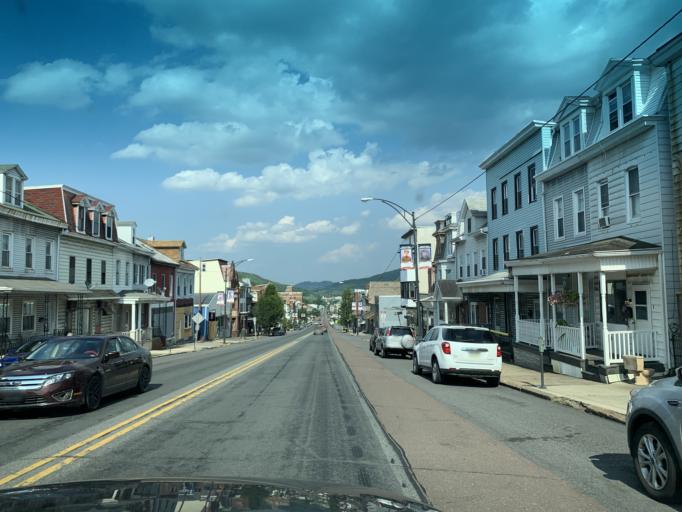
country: US
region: Pennsylvania
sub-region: Schuylkill County
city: Ashland
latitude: 40.7817
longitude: -76.3467
